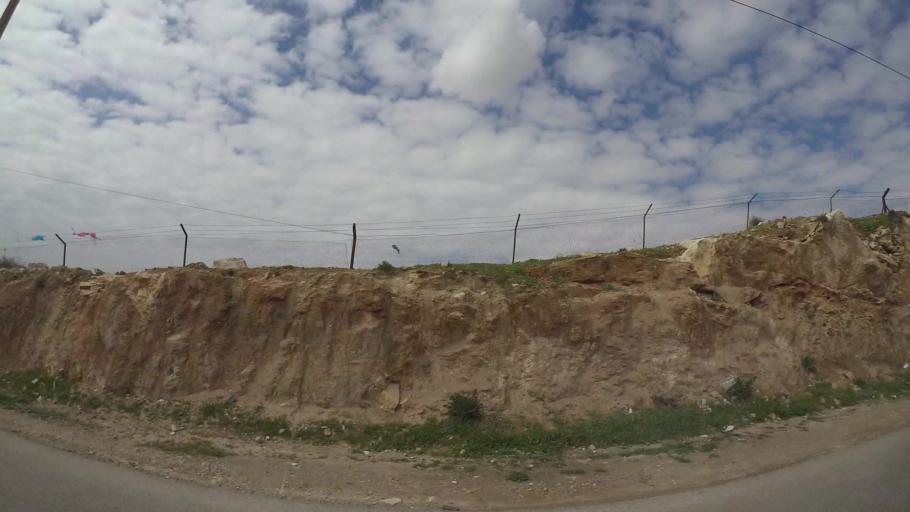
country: JO
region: Amman
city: Amman
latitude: 32.0013
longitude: 35.9149
